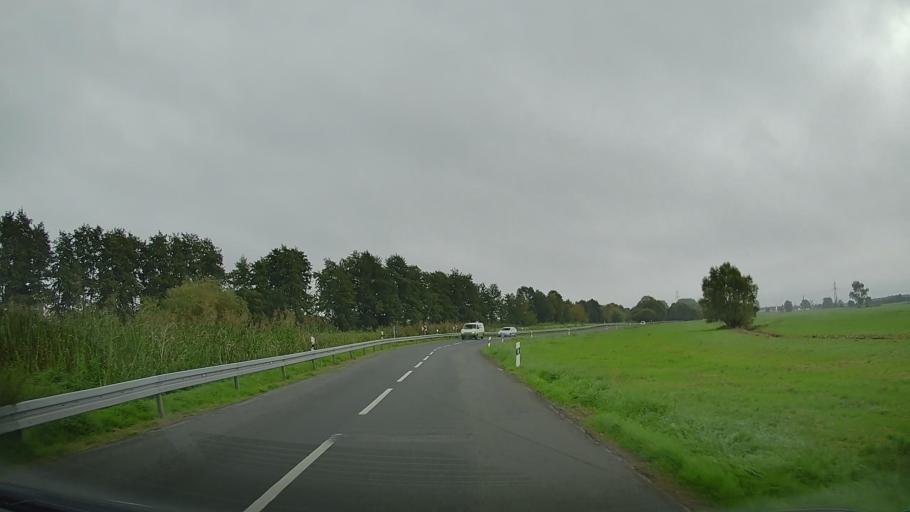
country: DE
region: Mecklenburg-Vorpommern
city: Guestrow
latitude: 53.8155
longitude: 12.1316
